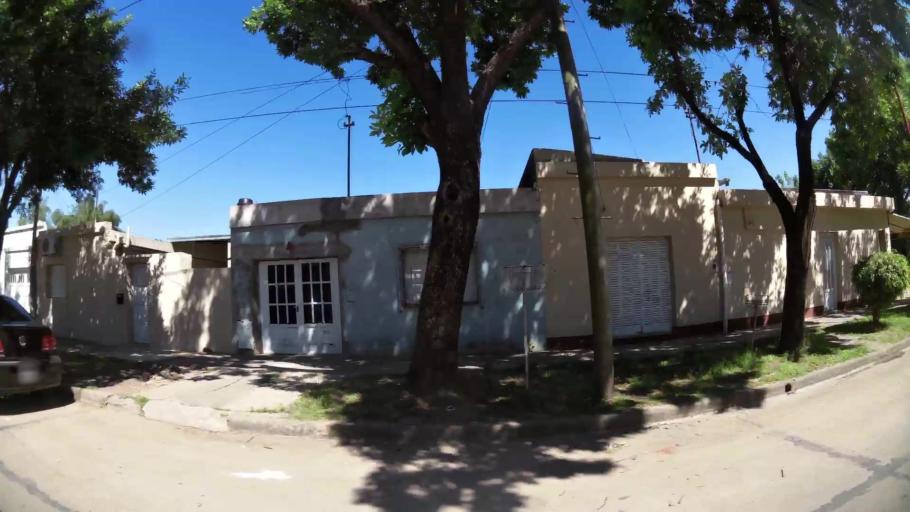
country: AR
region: Santa Fe
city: Esperanza
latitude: -31.4391
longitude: -60.9303
